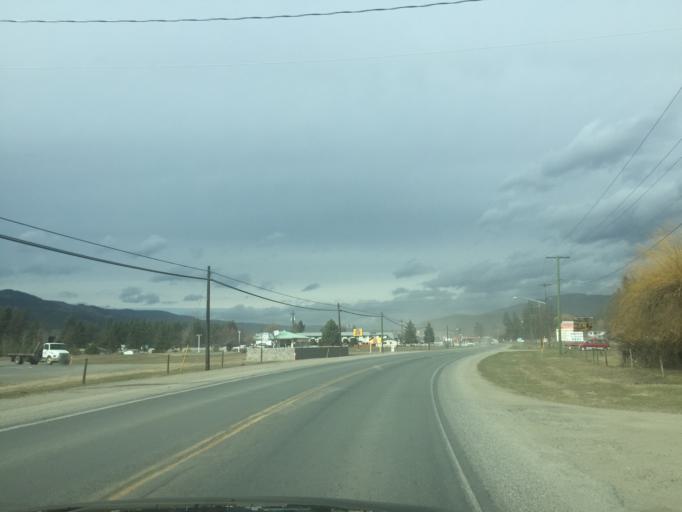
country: CA
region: British Columbia
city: Kamloops
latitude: 51.1680
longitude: -120.1264
